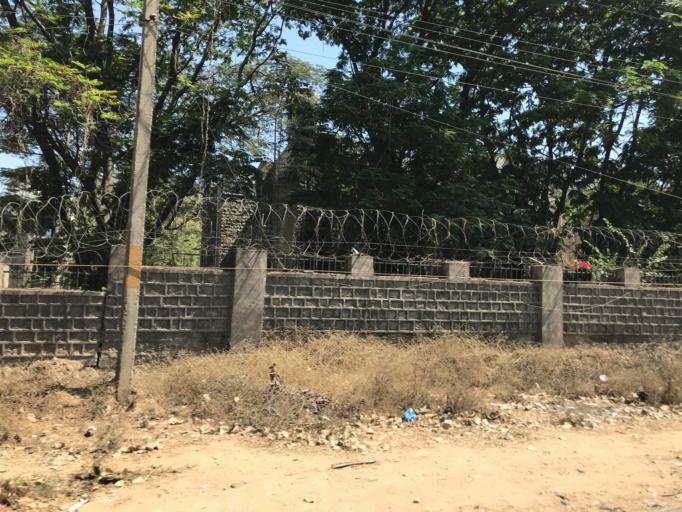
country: IN
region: Telangana
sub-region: Medak
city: Serilingampalle
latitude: 17.4674
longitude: 78.3319
